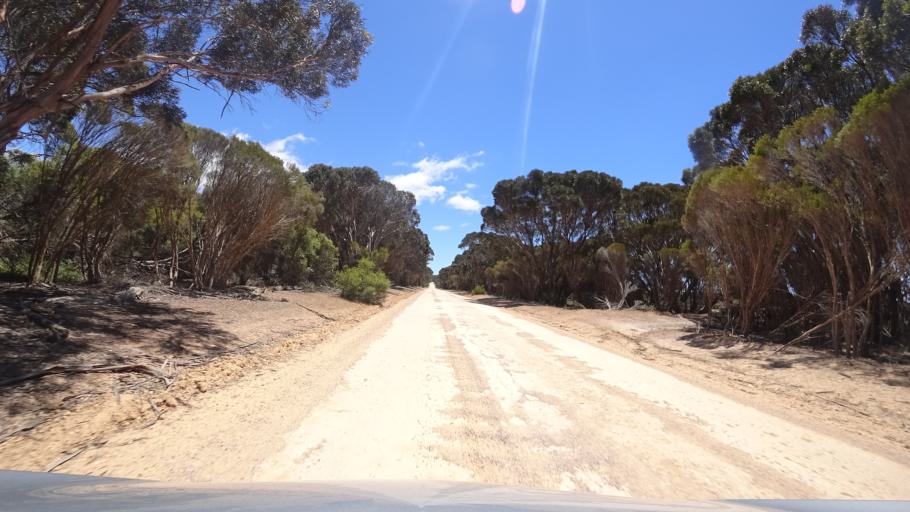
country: AU
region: South Australia
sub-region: Yankalilla
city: Normanville
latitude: -35.8262
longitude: 138.0818
